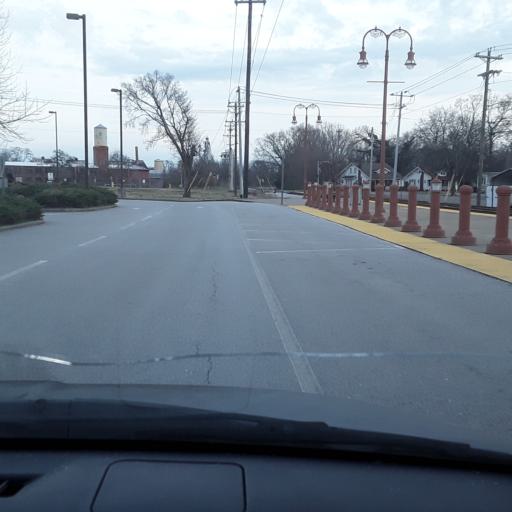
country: US
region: Tennessee
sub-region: Wilson County
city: Lebanon
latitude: 36.2121
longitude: -86.2972
